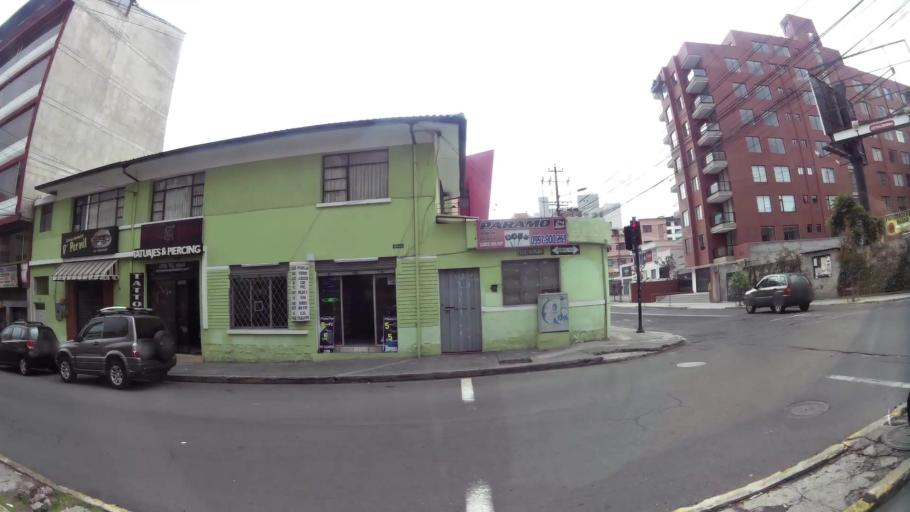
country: EC
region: Pichincha
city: Quito
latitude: -0.2086
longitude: -78.4857
